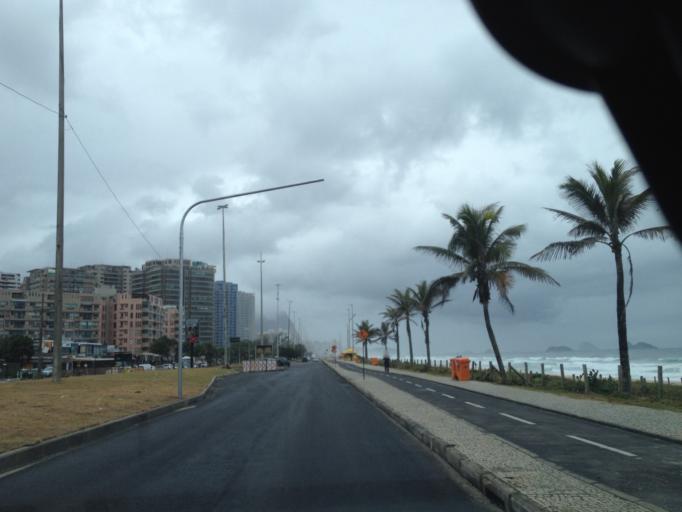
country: BR
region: Rio de Janeiro
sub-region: Rio De Janeiro
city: Rio de Janeiro
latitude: -23.0111
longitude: -43.3715
